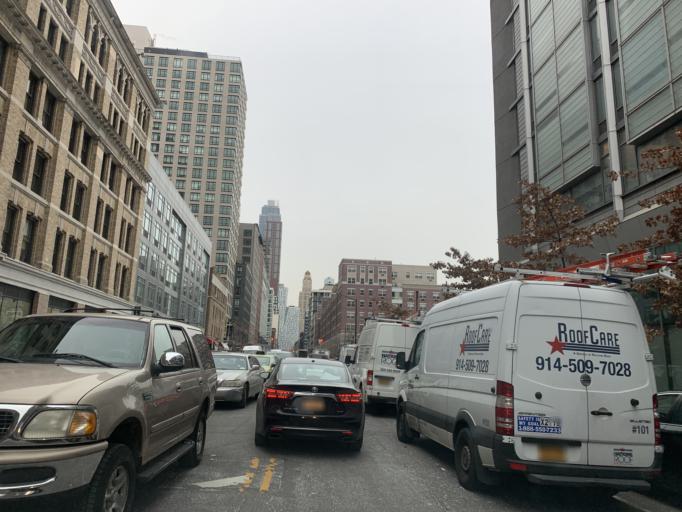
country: US
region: New York
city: New York City
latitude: 40.6895
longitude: -73.9874
